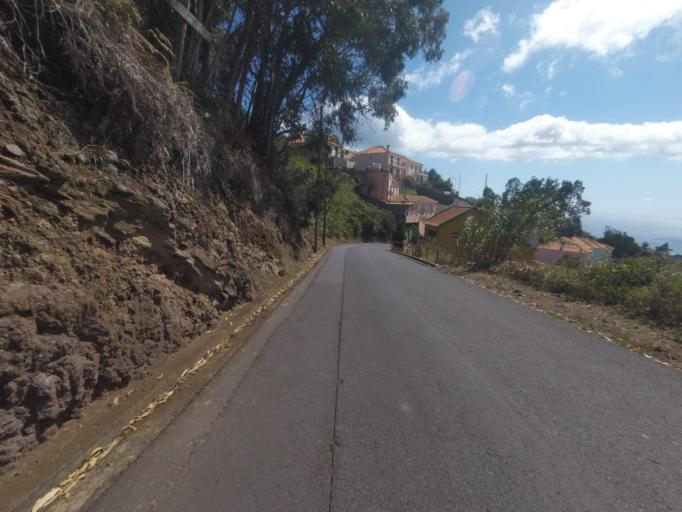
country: PT
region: Madeira
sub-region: Ribeira Brava
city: Campanario
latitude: 32.6790
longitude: -17.0431
